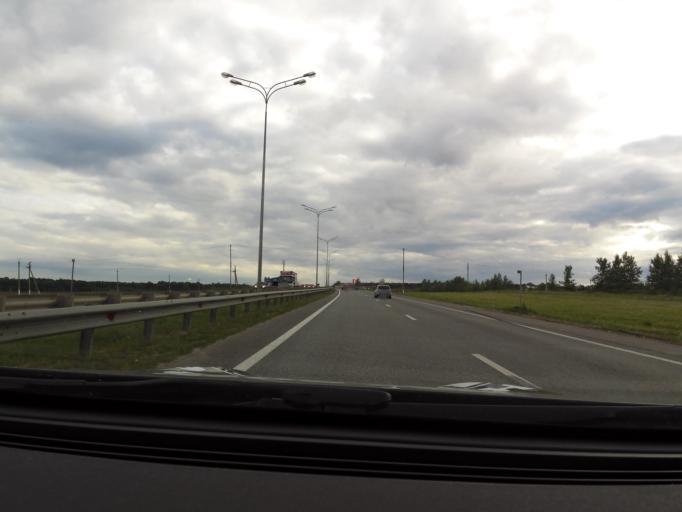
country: RU
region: Tatarstan
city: Osinovo
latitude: 55.7604
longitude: 48.8150
